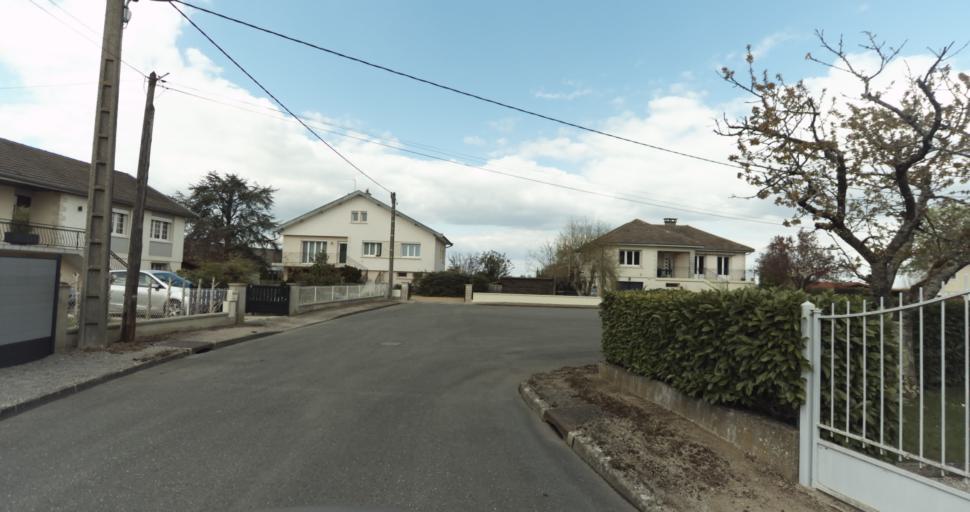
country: FR
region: Bourgogne
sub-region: Departement de la Cote-d'Or
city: Auxonne
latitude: 47.1970
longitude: 5.4041
